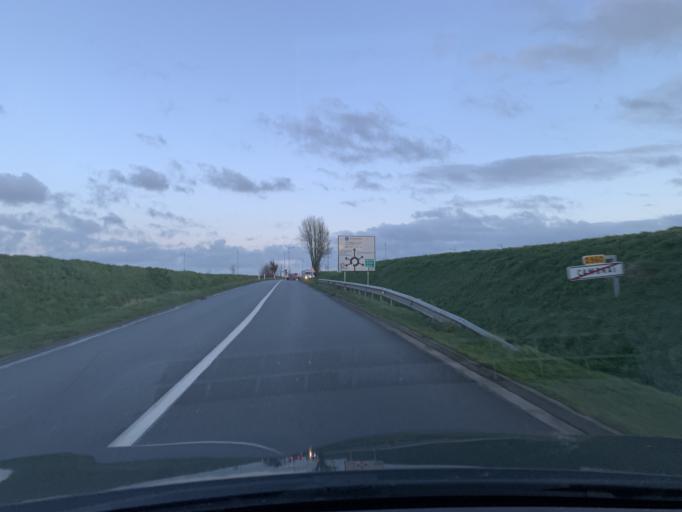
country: FR
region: Nord-Pas-de-Calais
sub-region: Departement du Nord
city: Cambrai
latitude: 50.1535
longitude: 3.2621
